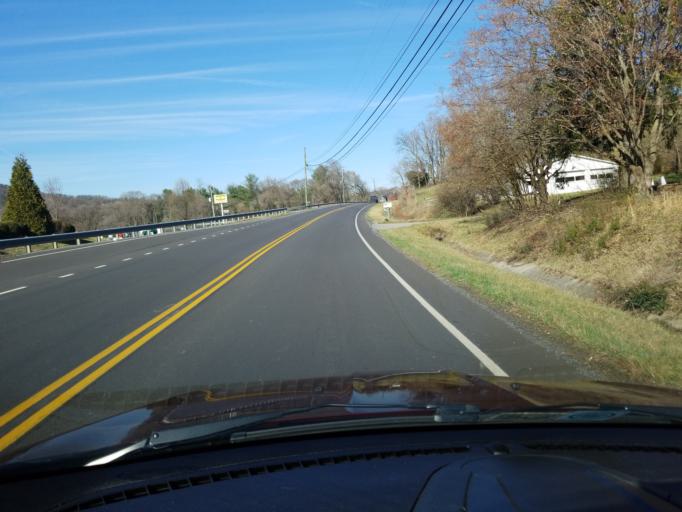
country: US
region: Virginia
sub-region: Botetourt County
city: Cloverdale
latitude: 37.3570
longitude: -79.9129
